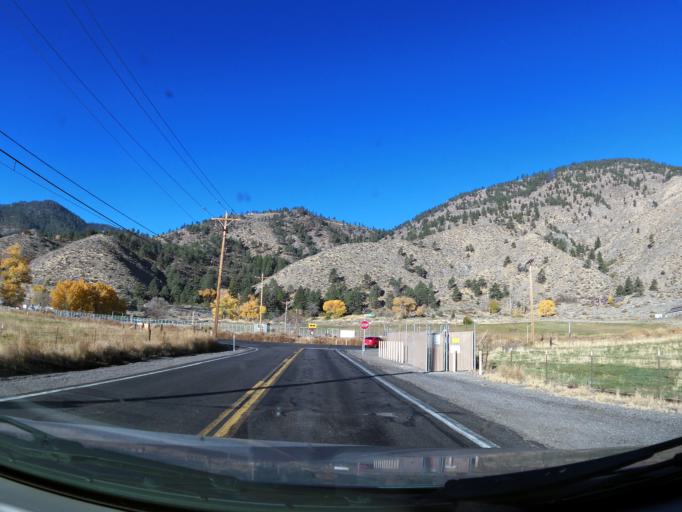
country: US
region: Nevada
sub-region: Douglas County
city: Kingsbury
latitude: 38.9711
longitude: -119.8374
